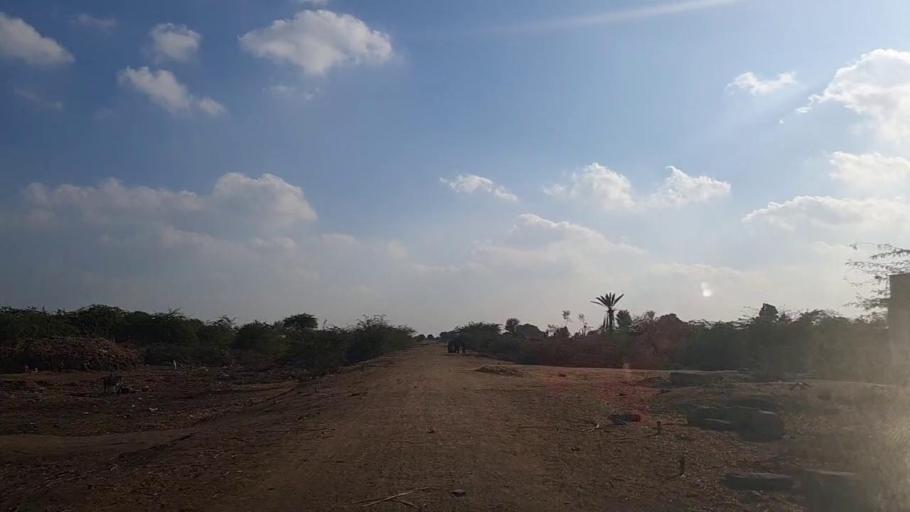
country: PK
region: Sindh
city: Tando Mittha Khan
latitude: 25.9451
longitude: 69.2119
